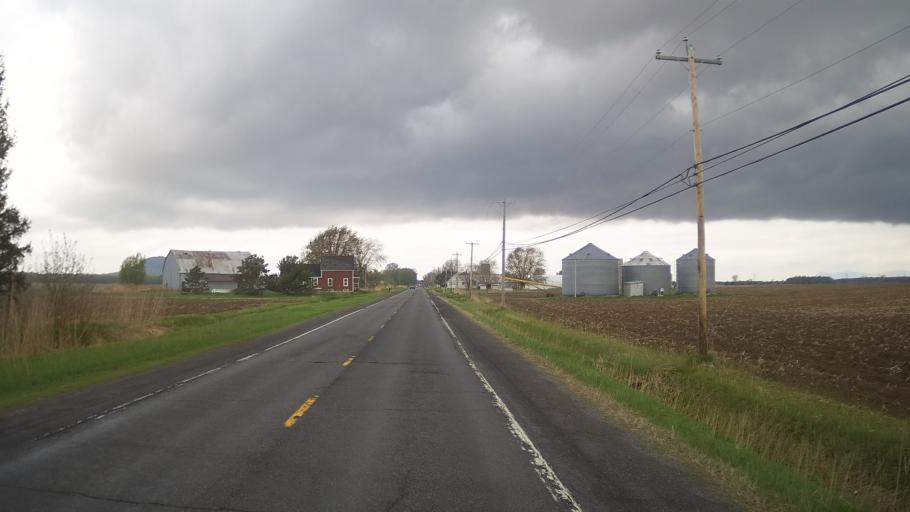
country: CA
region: Quebec
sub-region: Monteregie
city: Rougemont
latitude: 45.3333
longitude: -73.0795
